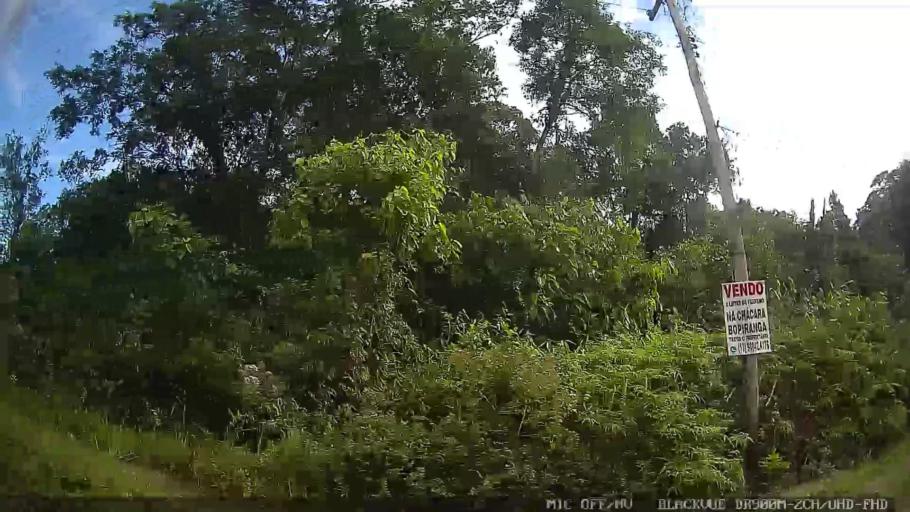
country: BR
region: Sao Paulo
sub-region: Itanhaem
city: Itanhaem
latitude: -24.1914
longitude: -46.9042
